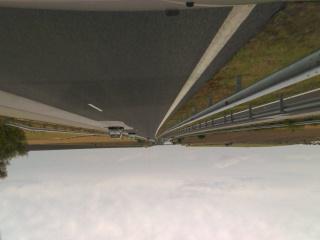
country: BG
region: Stara Zagora
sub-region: Obshtina Chirpan
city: Chirpan
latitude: 42.1989
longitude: 25.2726
